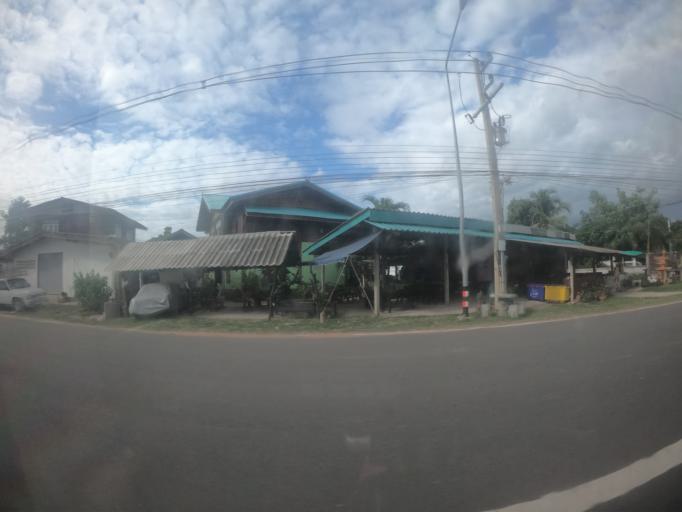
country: TH
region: Surin
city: Prasat
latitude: 14.6067
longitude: 103.4239
